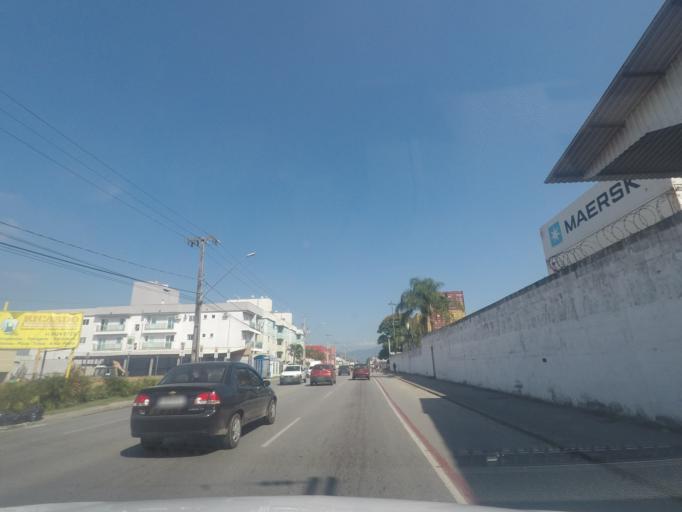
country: BR
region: Parana
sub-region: Paranagua
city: Paranagua
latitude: -25.5447
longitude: -48.5403
